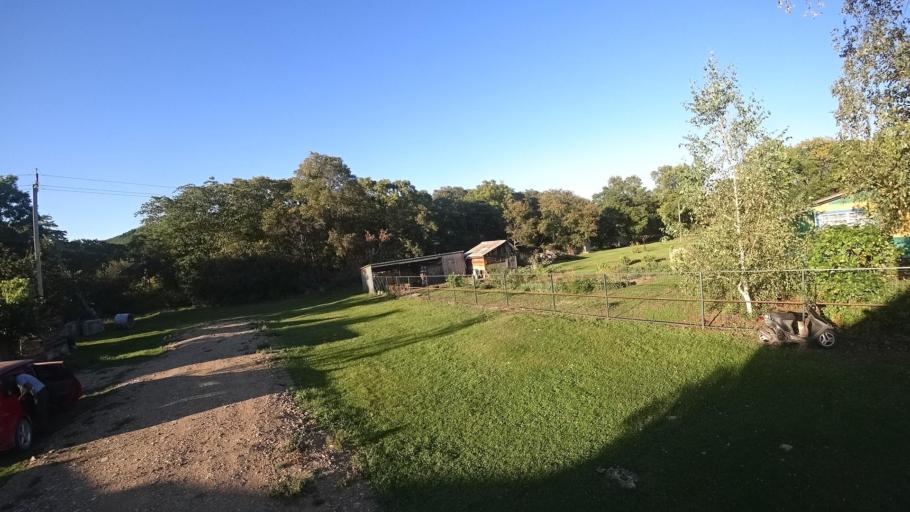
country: RU
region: Primorskiy
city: Kirovskiy
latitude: 44.8276
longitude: 133.5697
